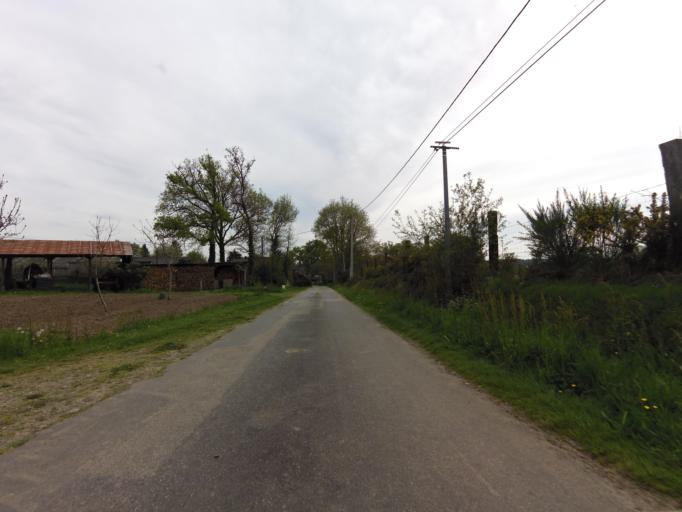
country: FR
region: Brittany
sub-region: Departement du Morbihan
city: Pluherlin
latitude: 47.7206
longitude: -2.3702
